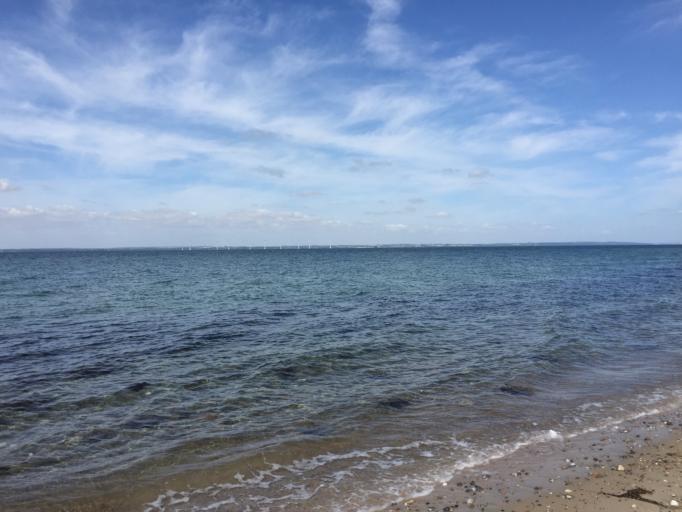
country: DK
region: Central Jutland
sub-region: Arhus Kommune
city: Beder
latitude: 55.9574
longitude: 10.4046
